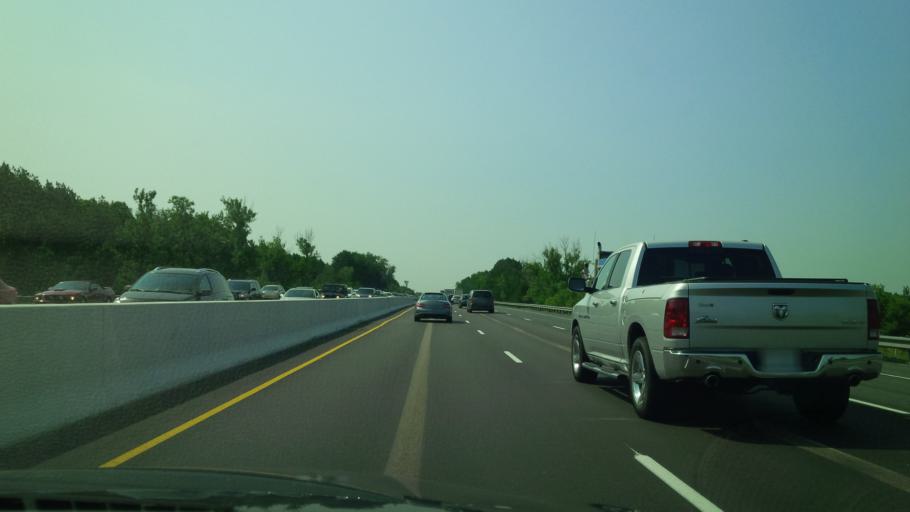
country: CA
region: Ontario
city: Bradford West Gwillimbury
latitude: 44.1610
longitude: -79.6433
